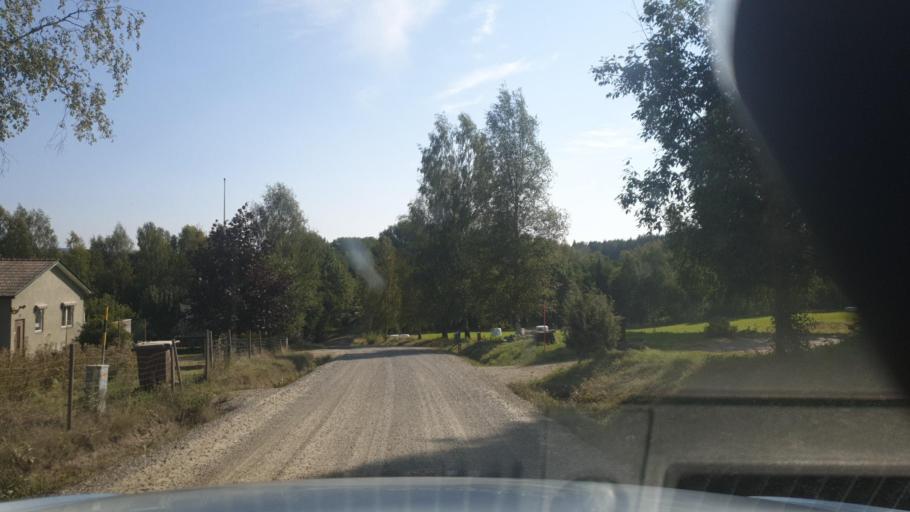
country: SE
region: Vaermland
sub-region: Arvika Kommun
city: Arvika
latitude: 59.8238
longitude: 12.5509
